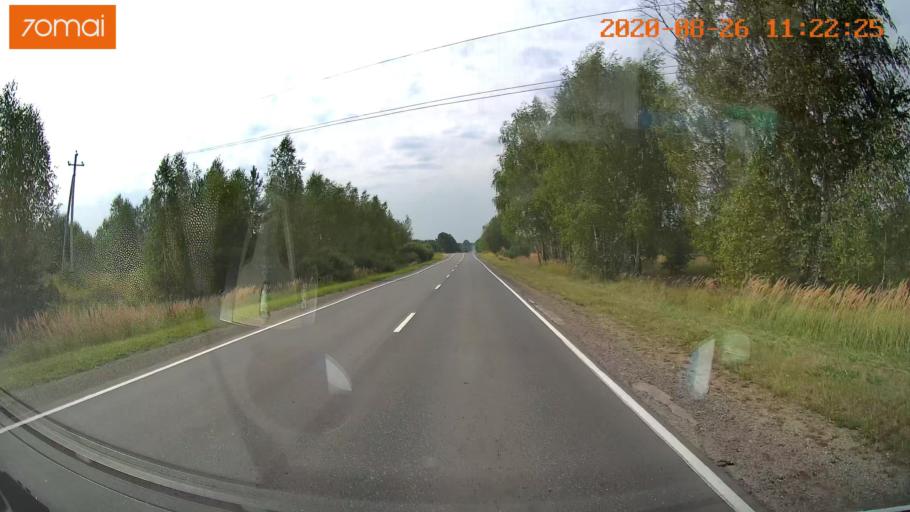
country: RU
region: Rjazan
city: Shilovo
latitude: 54.3642
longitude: 41.0275
